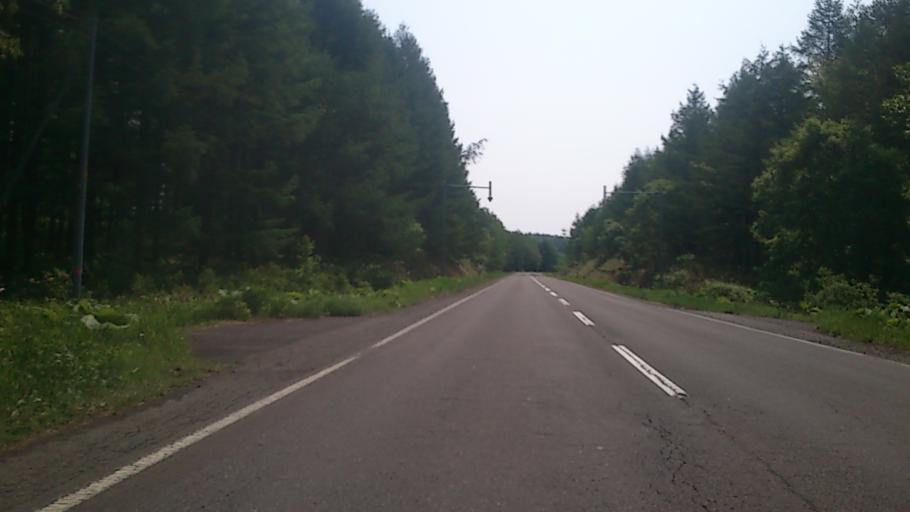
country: JP
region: Hokkaido
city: Kushiro
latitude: 43.4842
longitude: 144.5298
